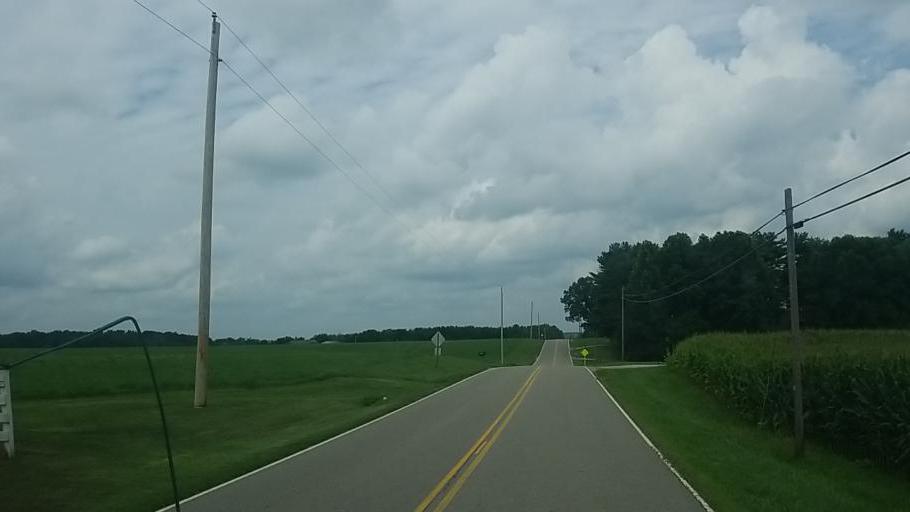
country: US
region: Ohio
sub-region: Licking County
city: Utica
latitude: 40.2147
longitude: -82.3665
